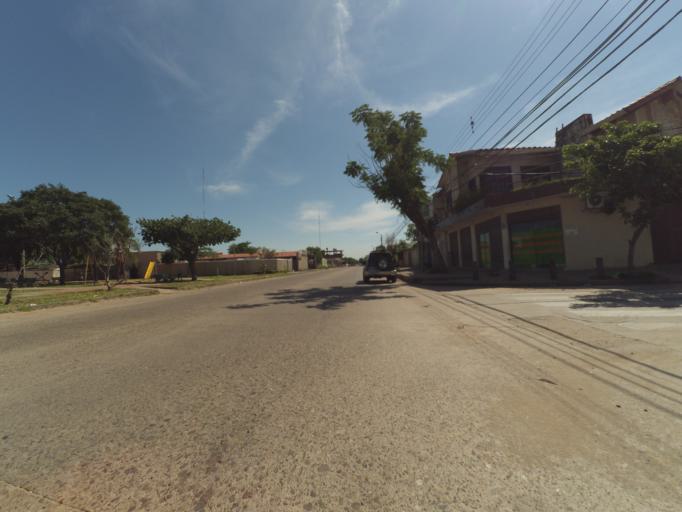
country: BO
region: Santa Cruz
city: Santa Cruz de la Sierra
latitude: -17.8098
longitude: -63.2022
